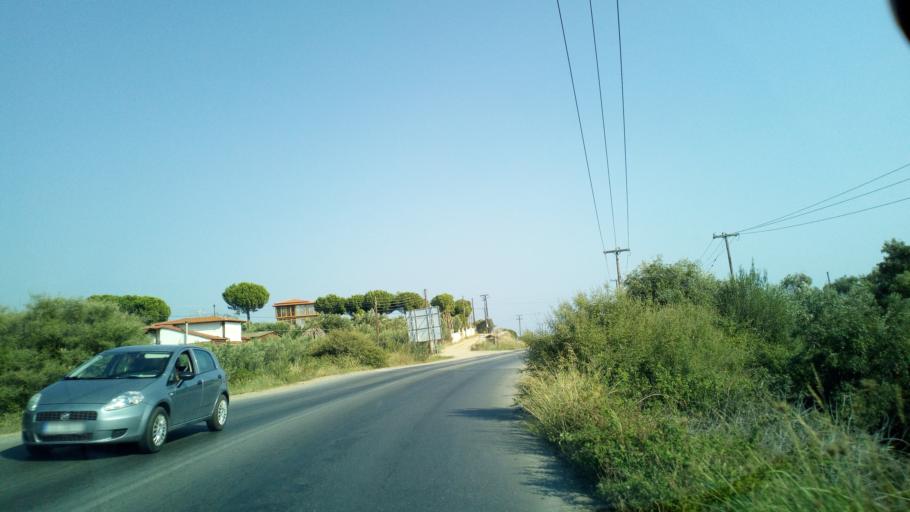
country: GR
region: Central Macedonia
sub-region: Nomos Chalkidikis
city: Kalyves Polygyrou
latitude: 40.2704
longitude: 23.4533
